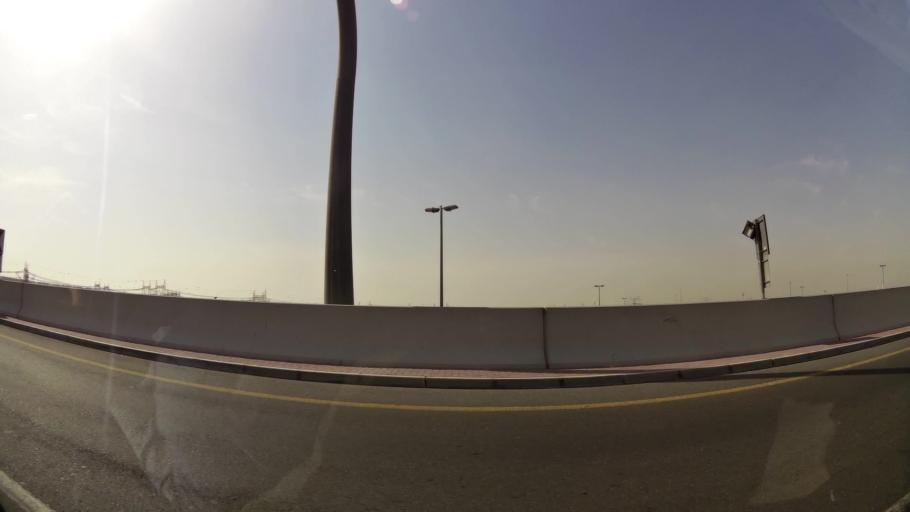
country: AE
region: Ash Shariqah
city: Sharjah
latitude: 25.2306
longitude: 55.4041
